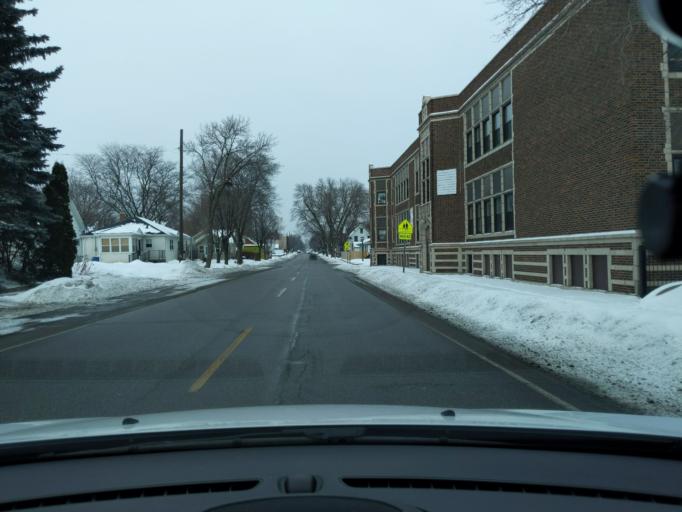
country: US
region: Minnesota
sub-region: Ramsey County
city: Falcon Heights
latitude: 44.9604
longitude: -93.1568
